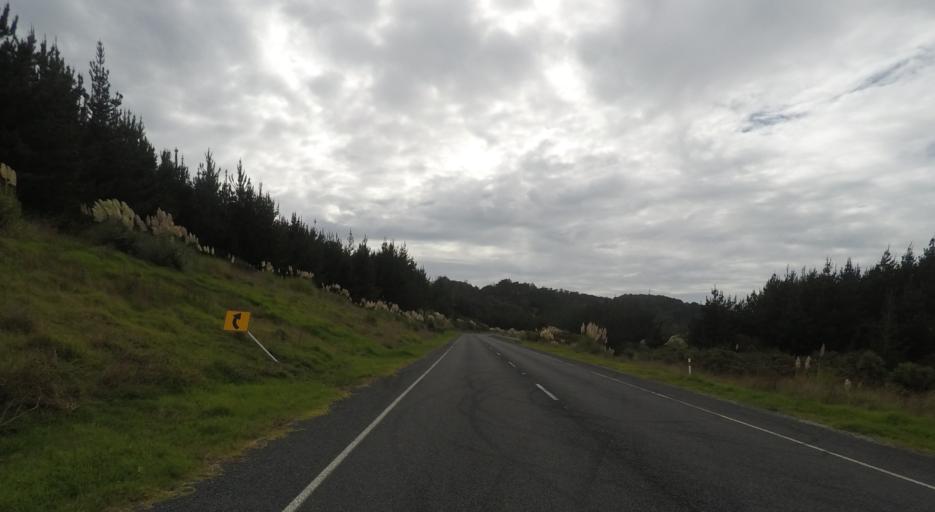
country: NZ
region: Auckland
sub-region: Auckland
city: Rothesay Bay
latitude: -36.6522
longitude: 174.7072
